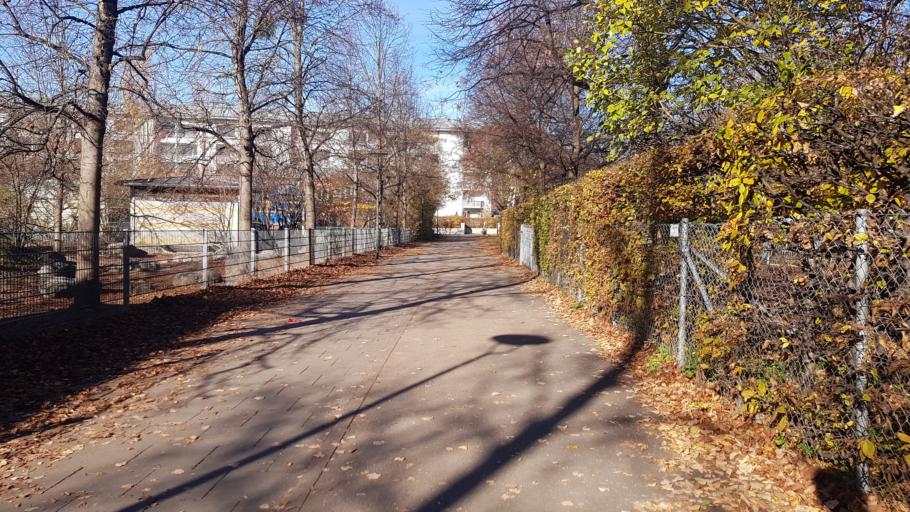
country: DE
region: Bavaria
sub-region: Upper Bavaria
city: Munich
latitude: 48.1638
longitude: 11.5472
